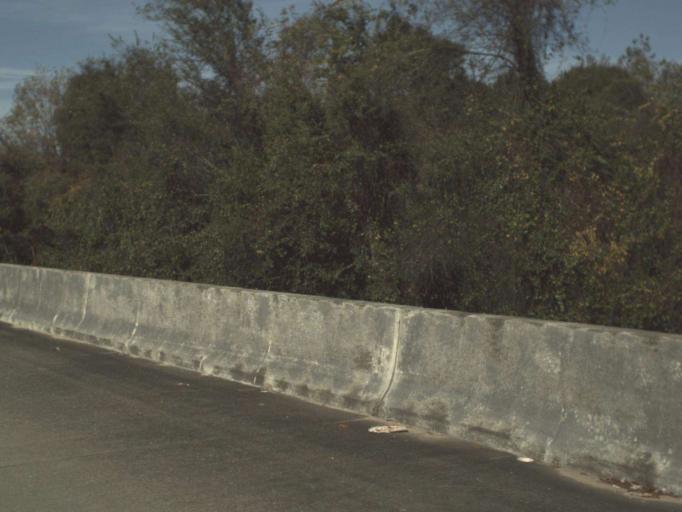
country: US
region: Florida
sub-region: Escambia County
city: Century
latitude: 30.9618
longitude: -87.2346
